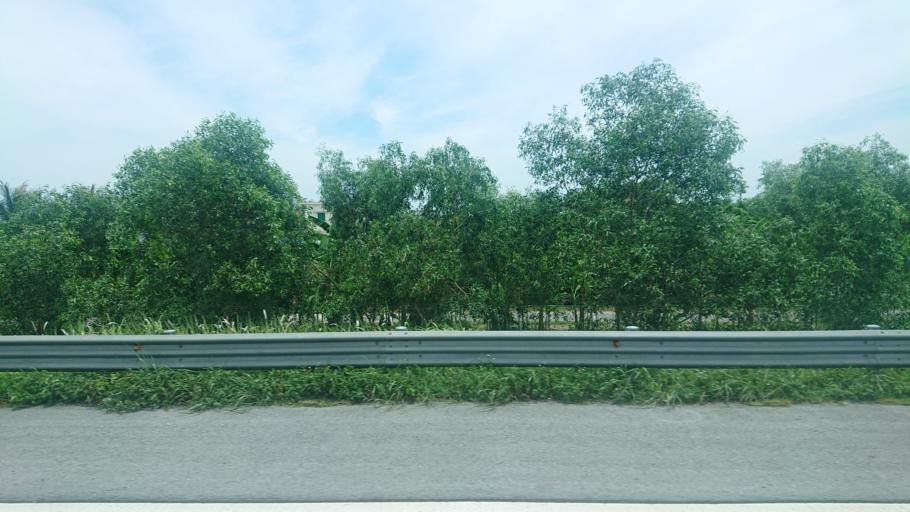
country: VN
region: Hai Phong
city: An Lao
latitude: 20.8121
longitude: 106.5019
